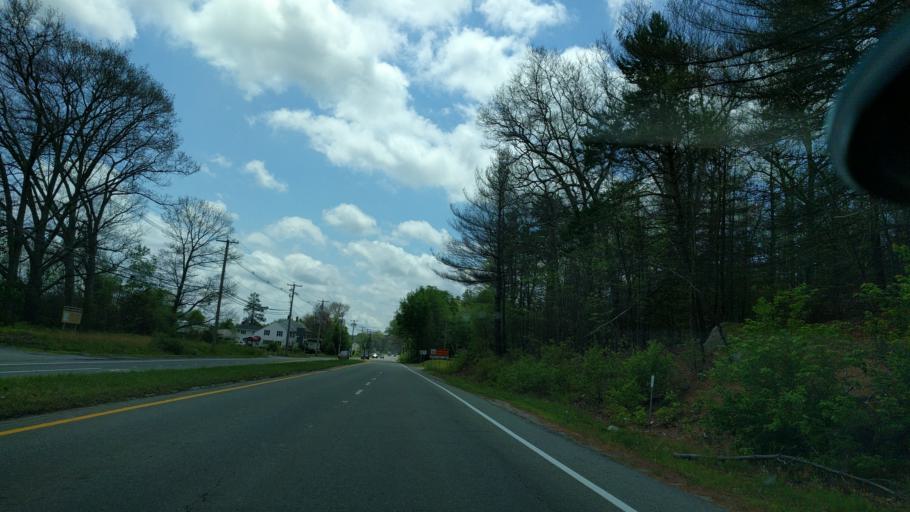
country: US
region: Massachusetts
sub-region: Worcester County
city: Uxbridge
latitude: 42.0430
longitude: -71.6219
